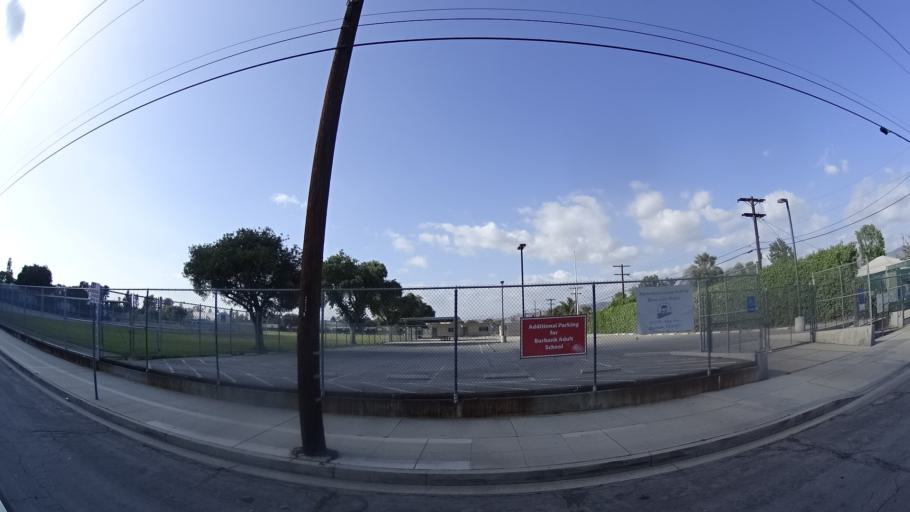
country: US
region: California
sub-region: Los Angeles County
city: North Hollywood
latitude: 34.1775
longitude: -118.3513
